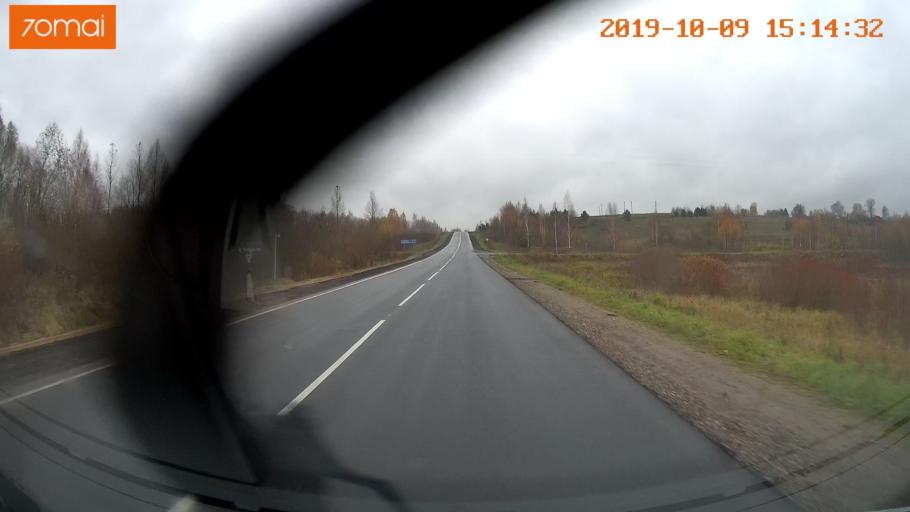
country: RU
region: Kostroma
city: Susanino
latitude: 58.1333
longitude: 41.6022
